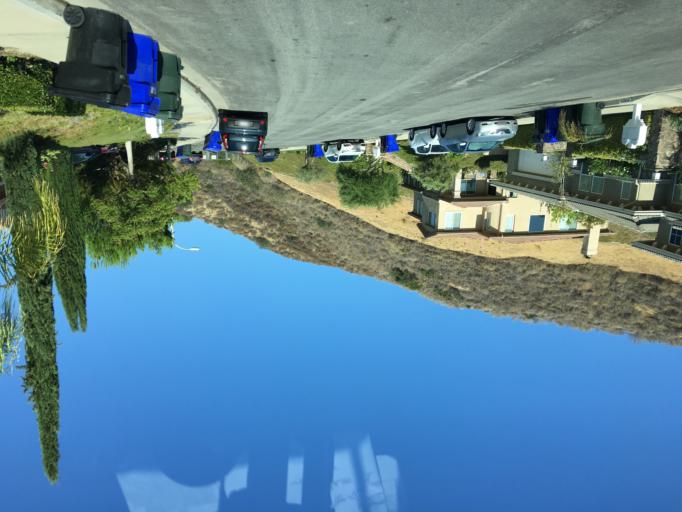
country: US
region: California
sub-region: Los Angeles County
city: Santa Clarita
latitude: 34.3745
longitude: -118.5933
